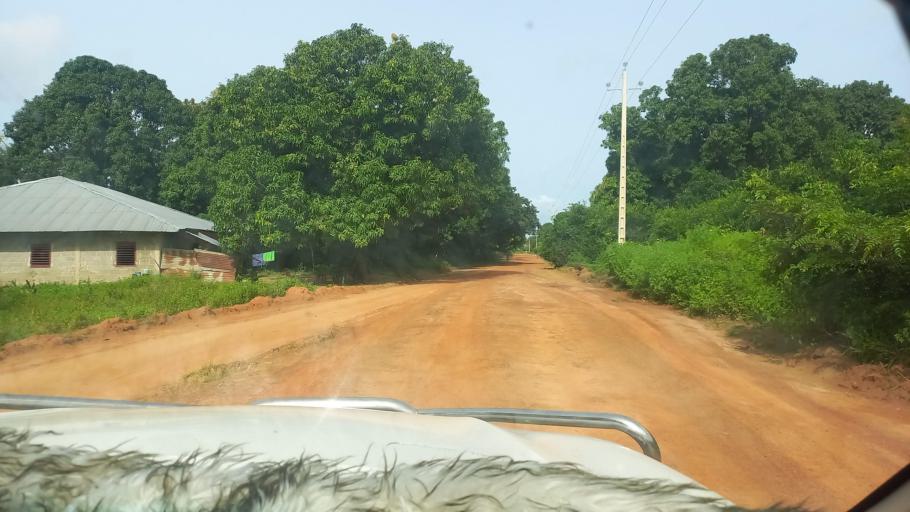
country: SN
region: Ziguinchor
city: Ziguinchor
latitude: 12.6699
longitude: -16.2719
